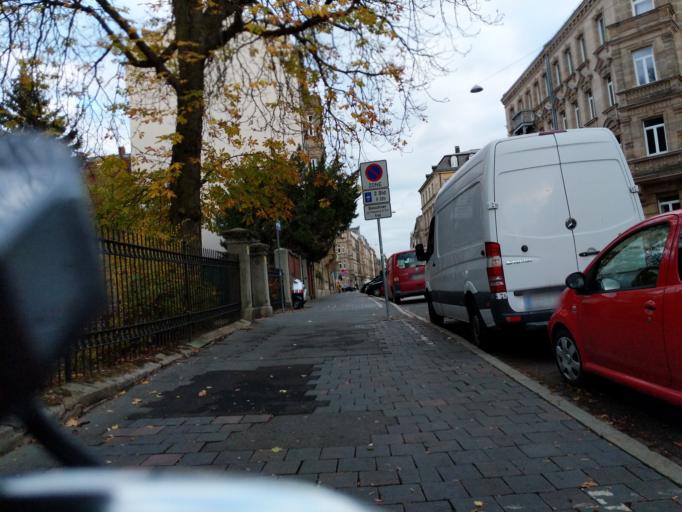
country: DE
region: Bavaria
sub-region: Regierungsbezirk Mittelfranken
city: Furth
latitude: 49.4689
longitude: 10.9850
